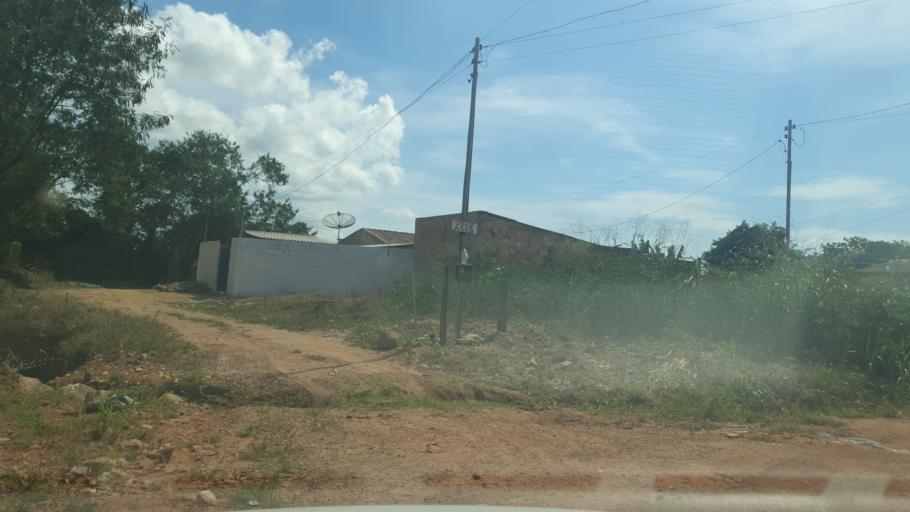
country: BR
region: Mato Grosso
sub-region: Pontes E Lacerda
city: Pontes e Lacerda
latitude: -15.2257
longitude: -59.3446
